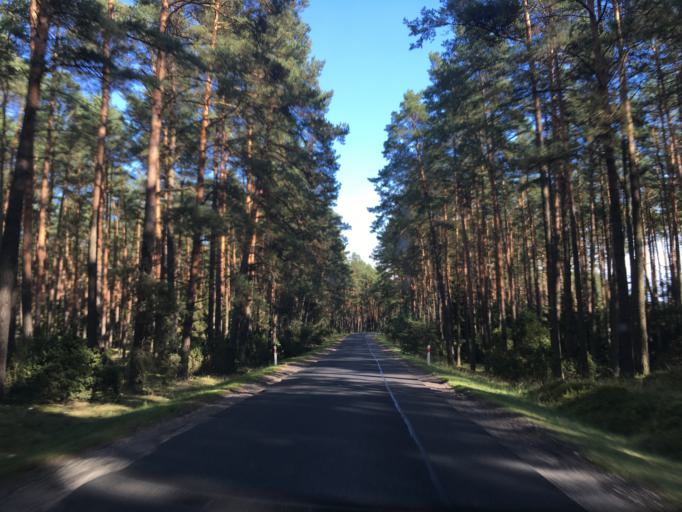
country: PL
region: Kujawsko-Pomorskie
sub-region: Powiat swiecki
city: Jezewo
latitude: 53.6135
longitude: 18.5286
